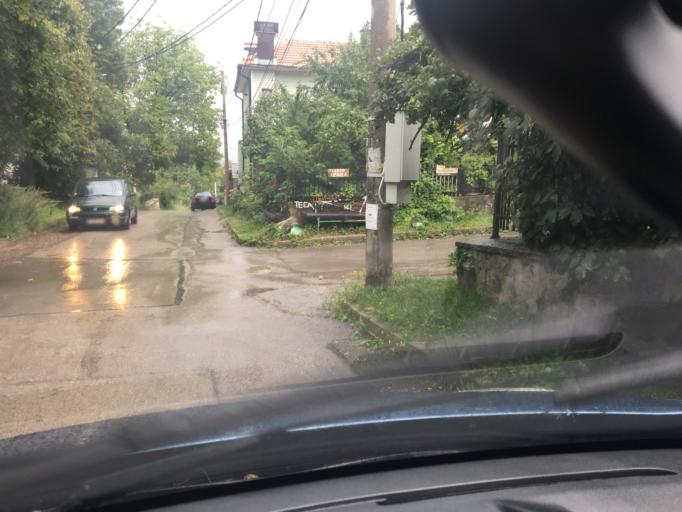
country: BG
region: Sofia-Capital
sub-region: Stolichna Obshtina
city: Sofia
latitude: 42.5871
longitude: 23.3517
